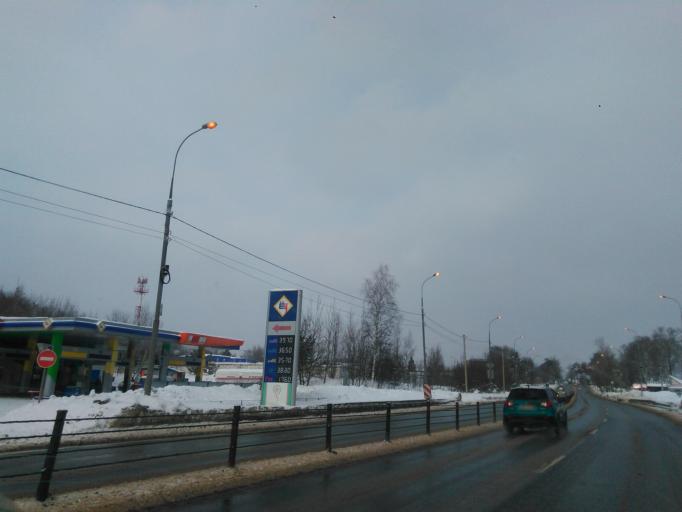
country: RU
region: Moskovskaya
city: Dedenevo
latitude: 56.2293
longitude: 37.5276
